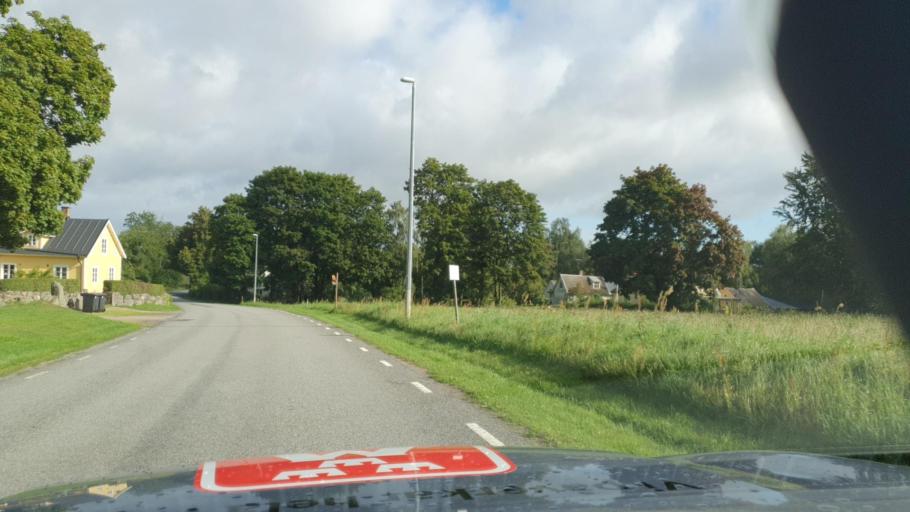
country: SE
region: Skane
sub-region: Hassleholms Kommun
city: Vinslov
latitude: 56.0588
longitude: 13.8359
